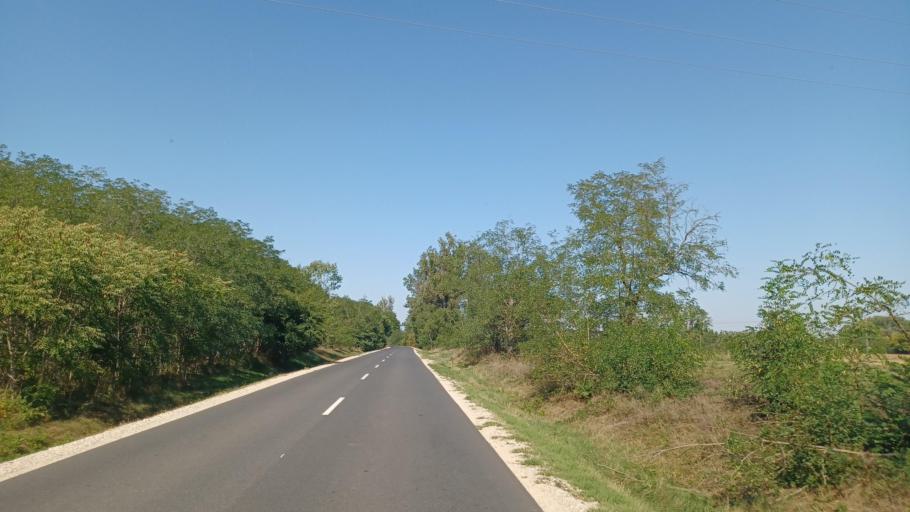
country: HU
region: Fejer
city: Alap
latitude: 46.7448
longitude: 18.6936
